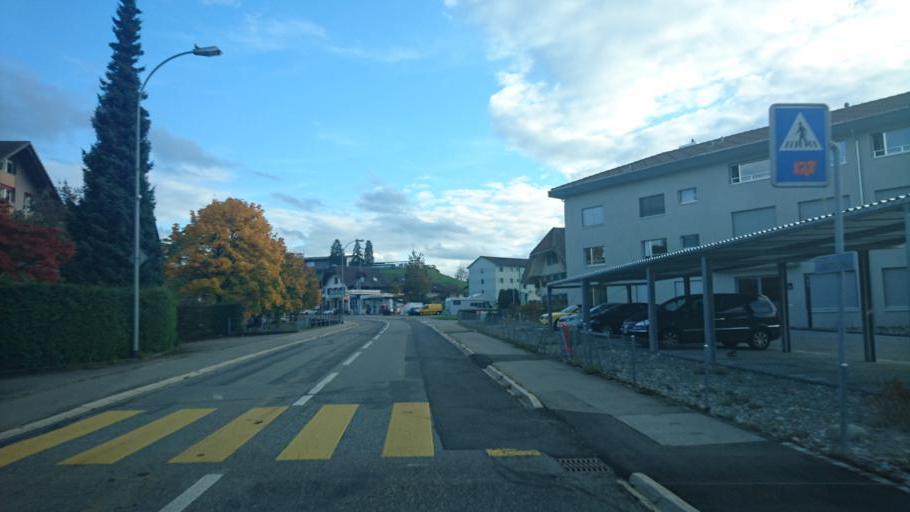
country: CH
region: Bern
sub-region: Bern-Mittelland District
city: Biglen
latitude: 46.9284
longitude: 7.6210
